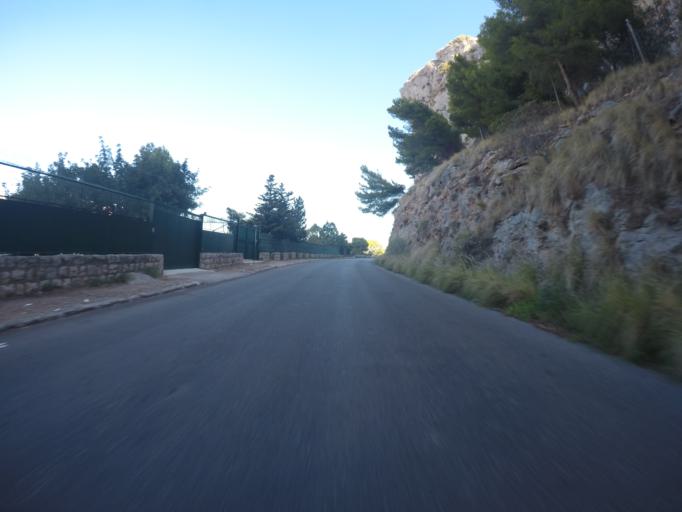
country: IT
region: Sicily
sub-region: Palermo
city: Palermo
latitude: 38.1939
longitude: 13.3377
